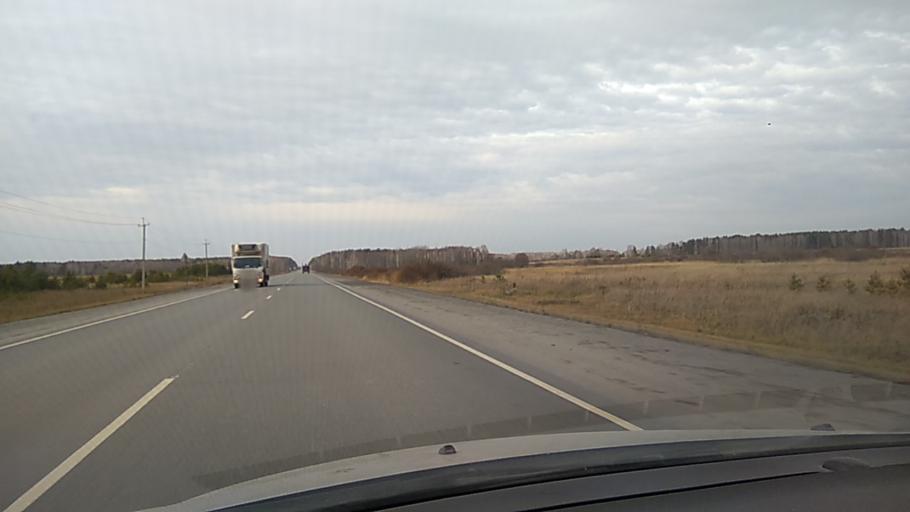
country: RU
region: Sverdlovsk
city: Troitskiy
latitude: 57.0893
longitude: 63.8616
